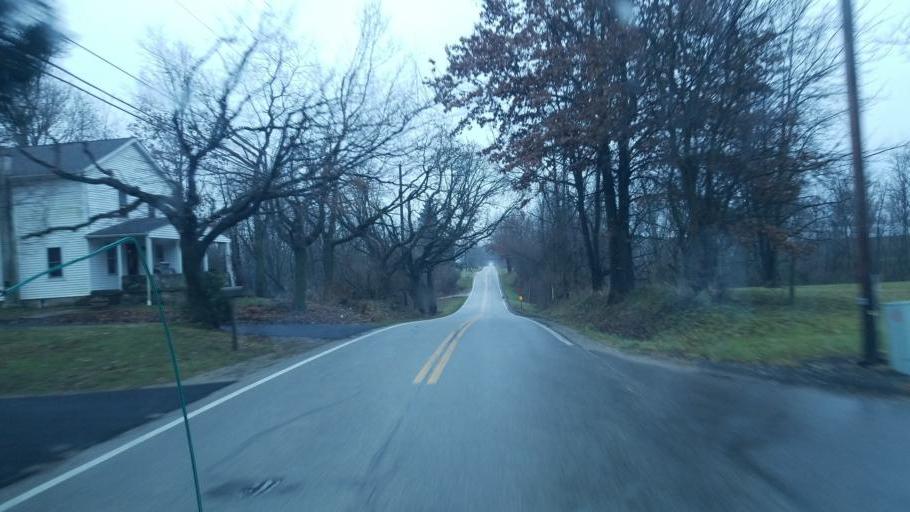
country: US
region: Ohio
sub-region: Delaware County
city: Delaware
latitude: 40.2821
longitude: -83.0471
